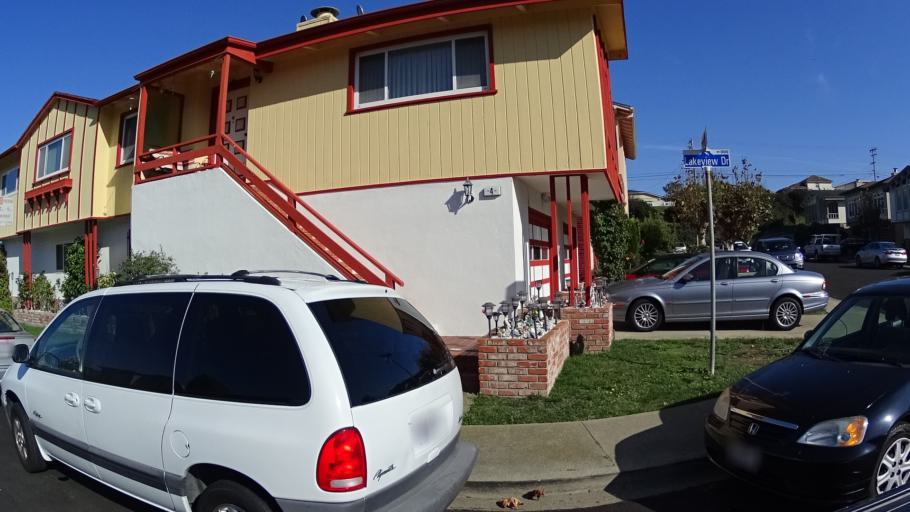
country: US
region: California
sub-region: San Mateo County
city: Broadmoor
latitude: 37.7058
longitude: -122.4844
